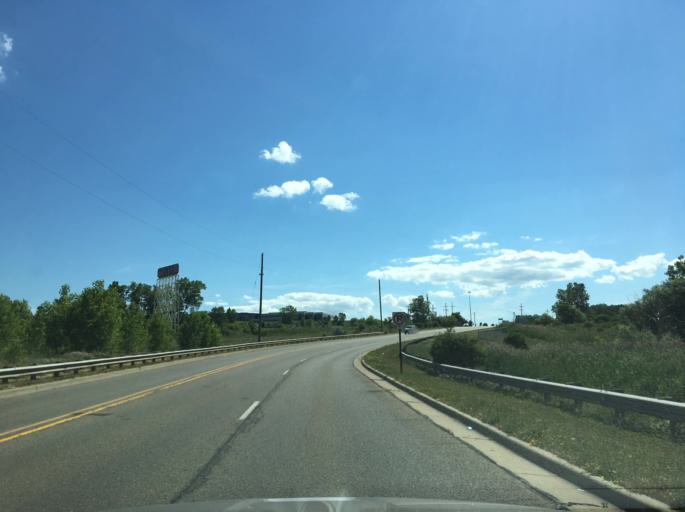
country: US
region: Michigan
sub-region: Oakland County
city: Auburn Hills
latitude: 42.6997
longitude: -83.2880
